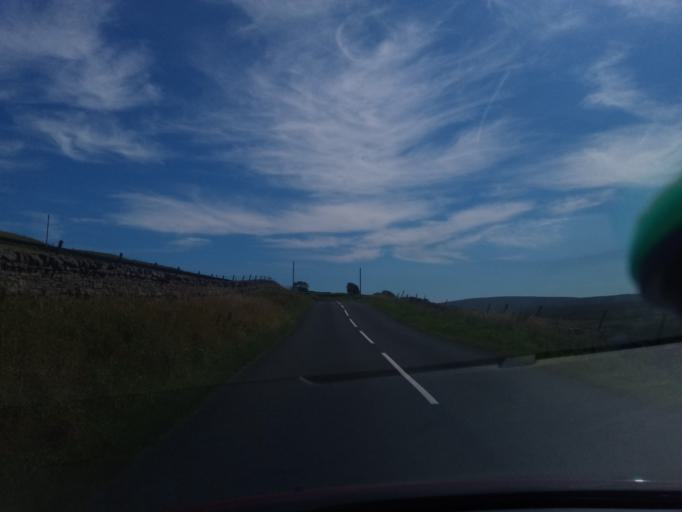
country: GB
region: England
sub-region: County Durham
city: Holwick
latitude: 54.7791
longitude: -2.2622
